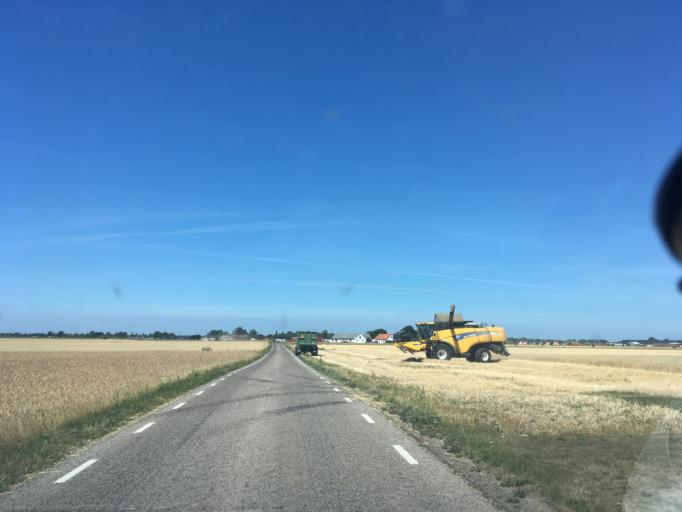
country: SE
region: Skane
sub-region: Trelleborgs Kommun
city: Skare
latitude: 55.3974
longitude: 13.0234
